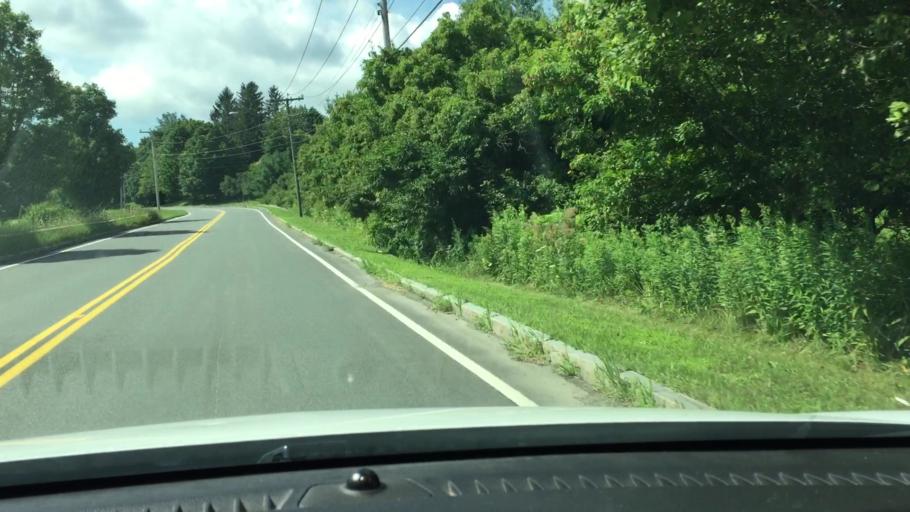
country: US
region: Massachusetts
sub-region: Berkshire County
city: Pittsfield
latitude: 42.4440
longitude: -73.3010
